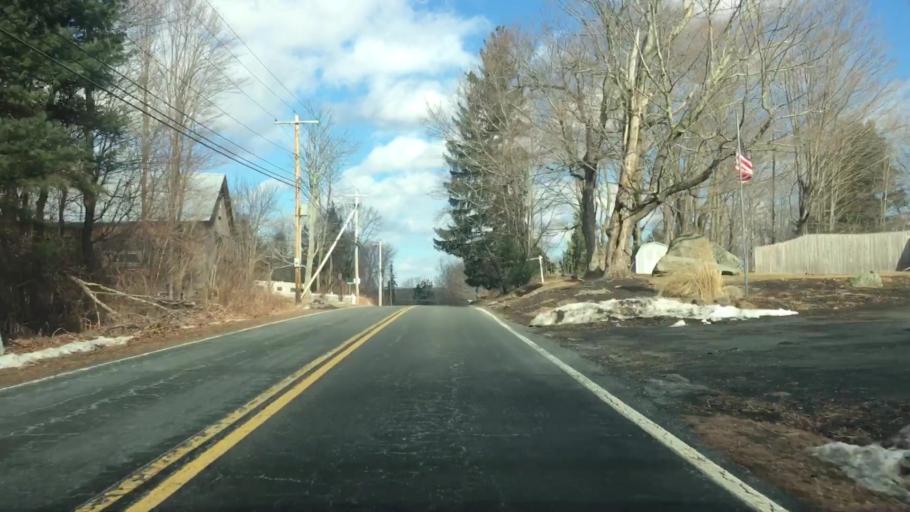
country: US
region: Massachusetts
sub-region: Hampden County
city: Wales
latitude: 42.0568
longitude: -72.2259
